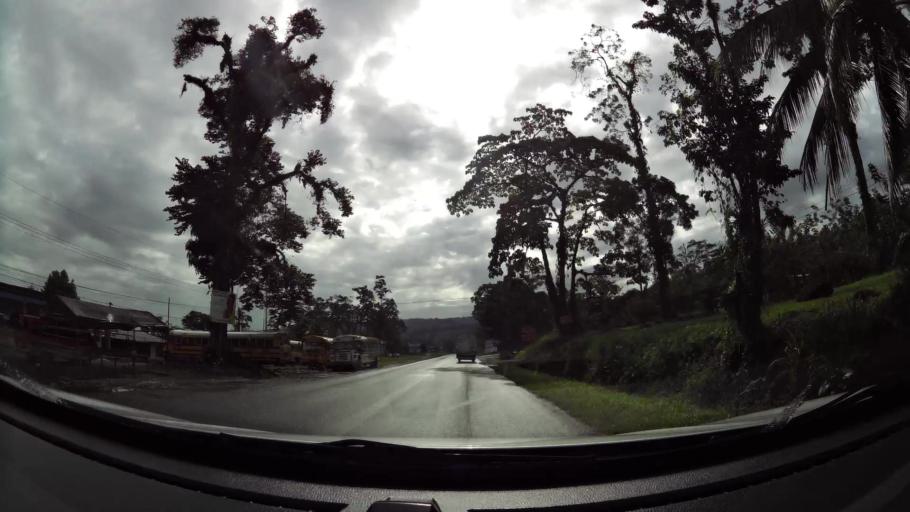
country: CR
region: Limon
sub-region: Canton de Siquirres
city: Siquirres
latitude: 10.0992
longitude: -83.5163
